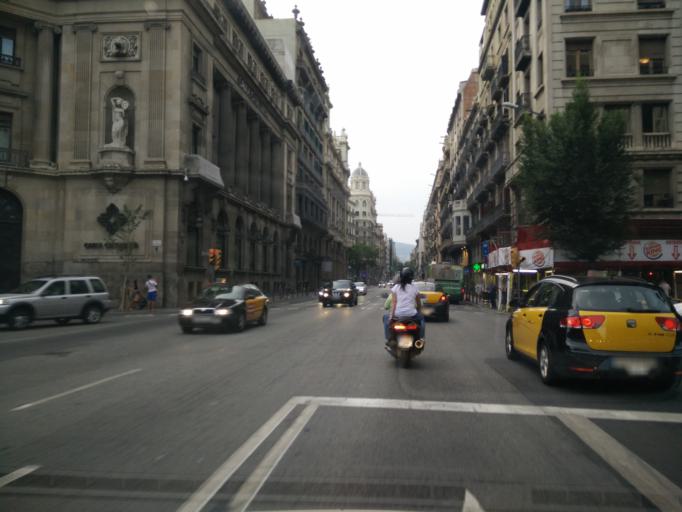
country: ES
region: Catalonia
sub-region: Provincia de Barcelona
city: Ciutat Vella
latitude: 41.3855
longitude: 2.1767
